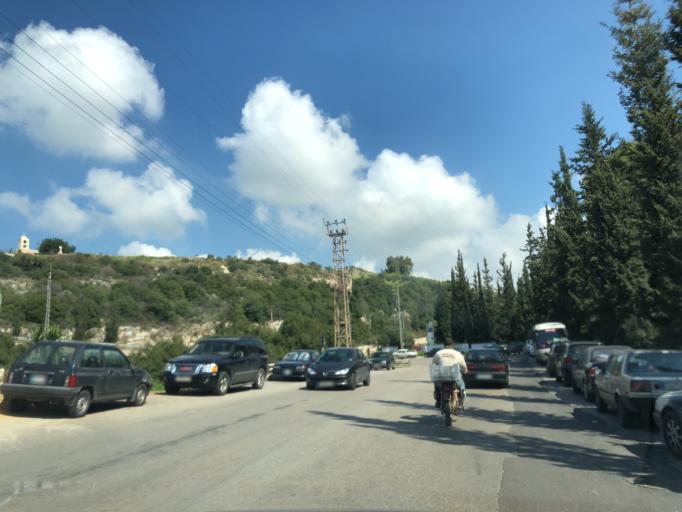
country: LB
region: Mont-Liban
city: Jbail
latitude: 34.1289
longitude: 35.6581
